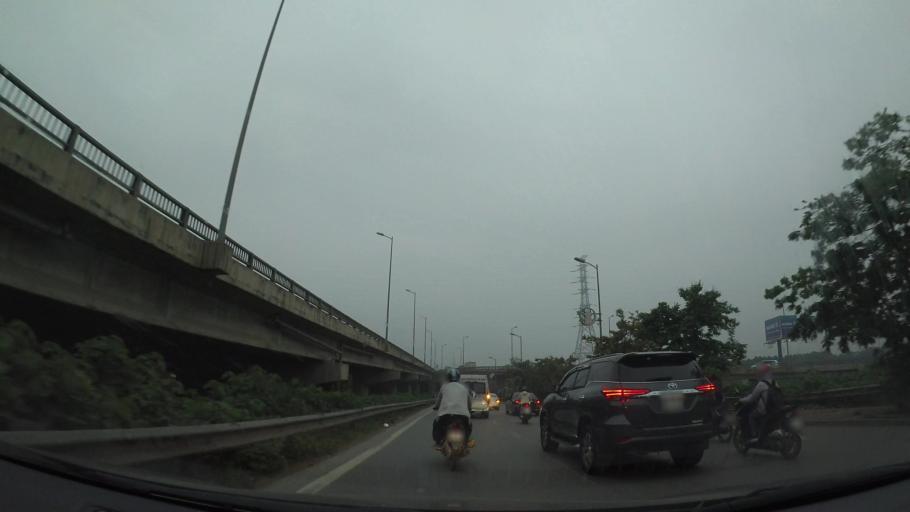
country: VN
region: Ha Noi
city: Van Dien
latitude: 20.9656
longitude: 105.8476
